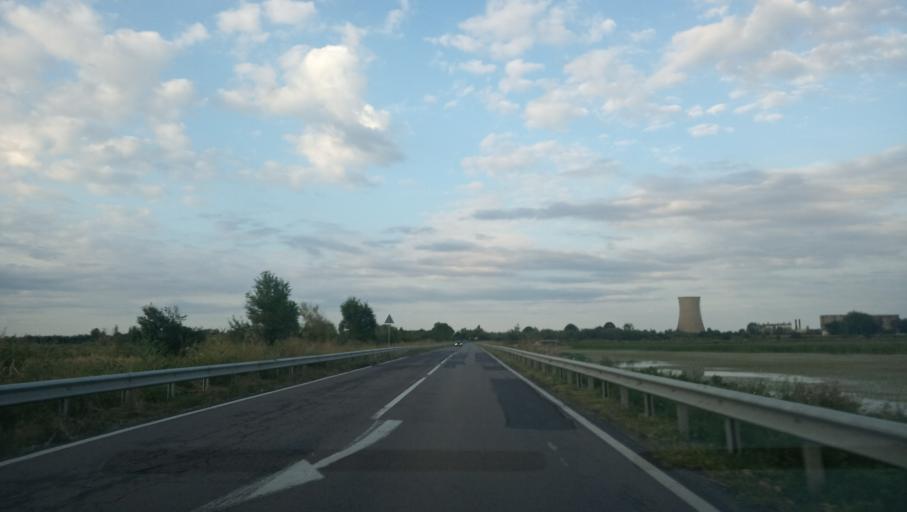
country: RO
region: Calarasi
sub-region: Comuna Cuza Voda
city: Cuza Voda
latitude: 44.2275
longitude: 27.2766
